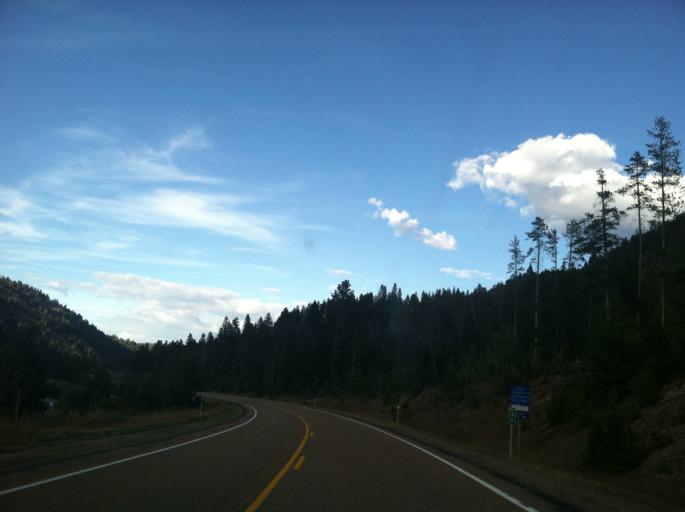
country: US
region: Montana
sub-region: Granite County
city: Philipsburg
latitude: 46.4243
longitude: -113.2758
